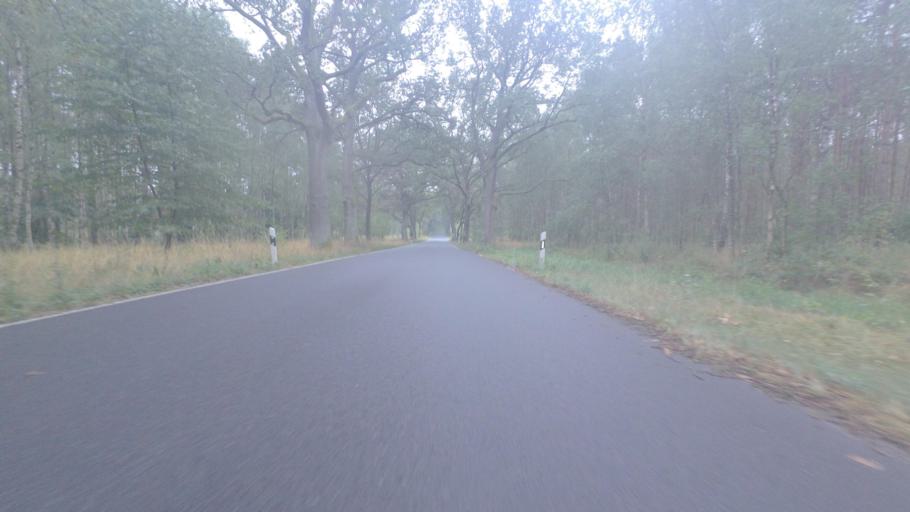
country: DE
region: Brandenburg
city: Heiligengrabe
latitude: 53.1584
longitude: 12.3456
